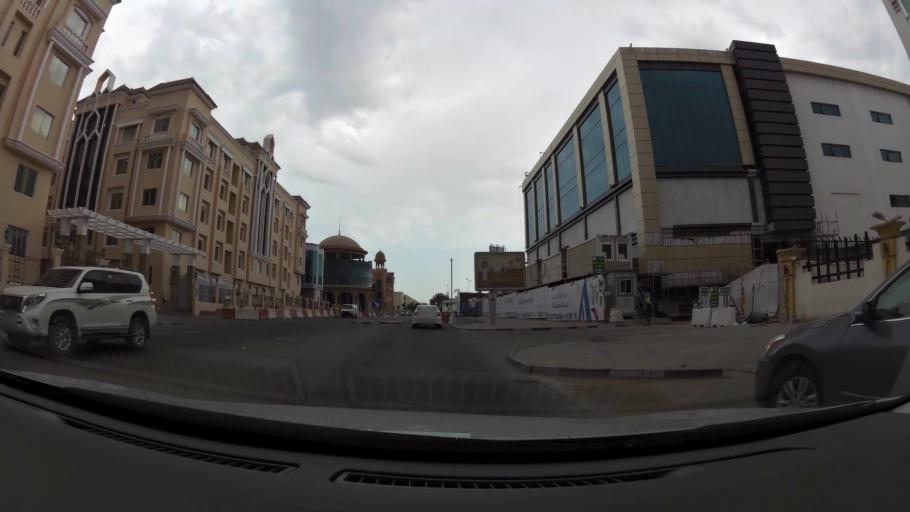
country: QA
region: Baladiyat ad Dawhah
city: Doha
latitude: 25.2748
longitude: 51.4981
